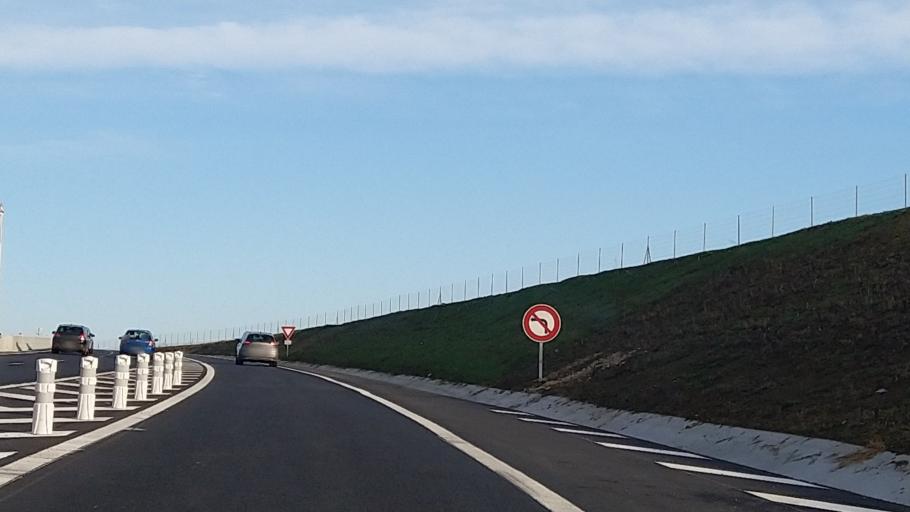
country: FR
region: Ile-de-France
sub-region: Departement du Val-d'Oise
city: Montsoult
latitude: 49.0715
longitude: 2.3324
